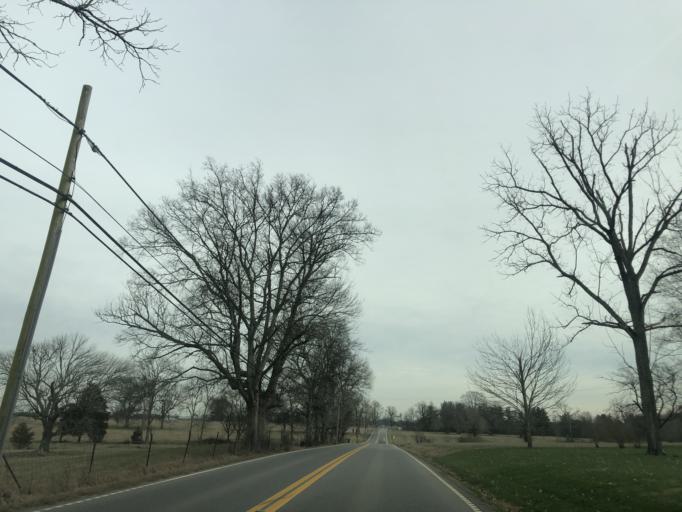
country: US
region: Tennessee
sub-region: Sumner County
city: Gallatin
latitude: 36.4075
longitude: -86.4991
